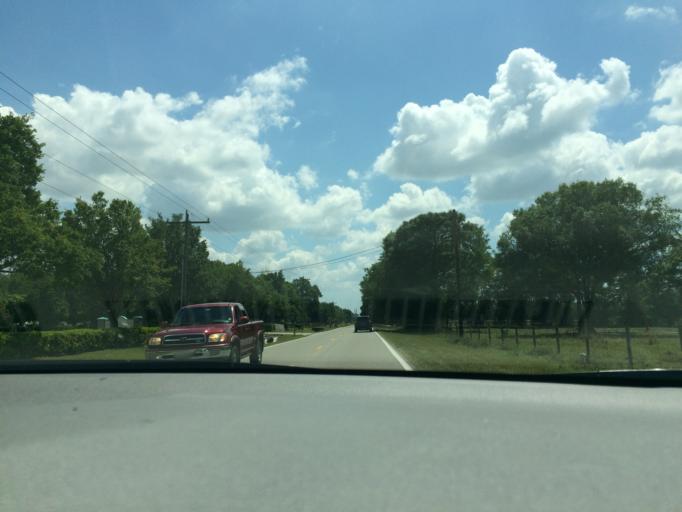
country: US
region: Florida
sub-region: Sarasota County
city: The Meadows
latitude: 27.4478
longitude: -82.3954
